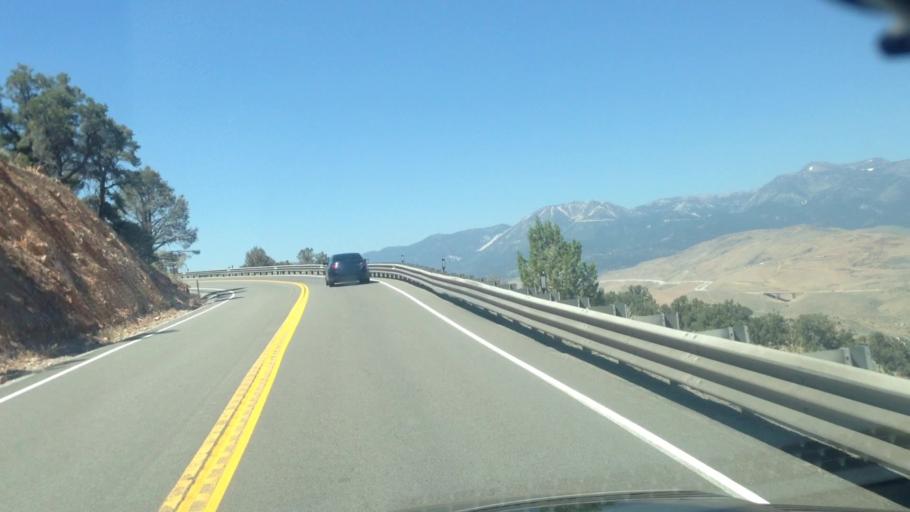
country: US
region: Nevada
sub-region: Storey County
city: Virginia City
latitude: 39.3859
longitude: -119.7014
